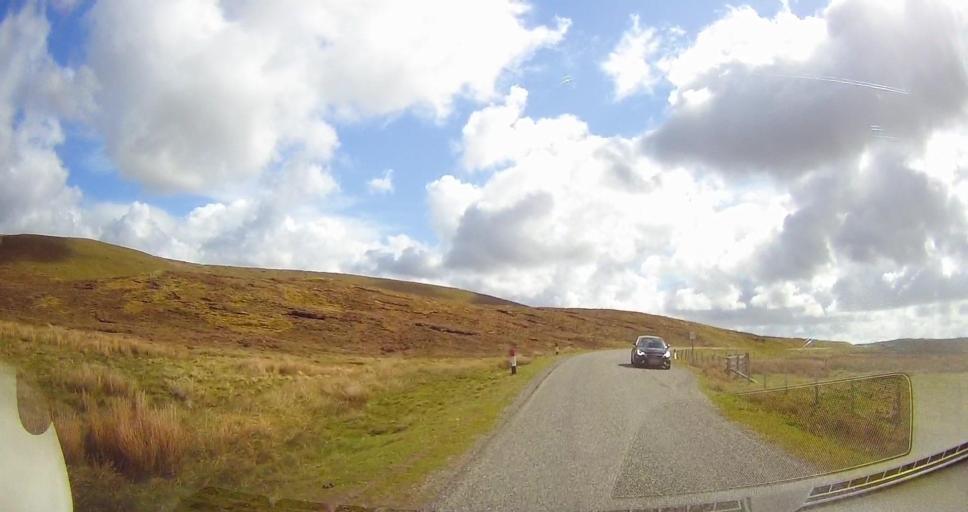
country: GB
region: Scotland
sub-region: Shetland Islands
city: Lerwick
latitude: 60.5175
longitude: -1.3776
